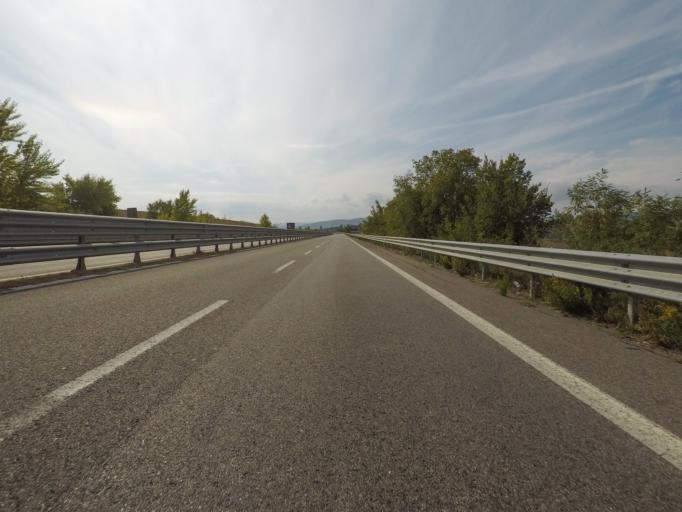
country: IT
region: Tuscany
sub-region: Provincia di Siena
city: Rosia
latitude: 43.2368
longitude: 11.2787
